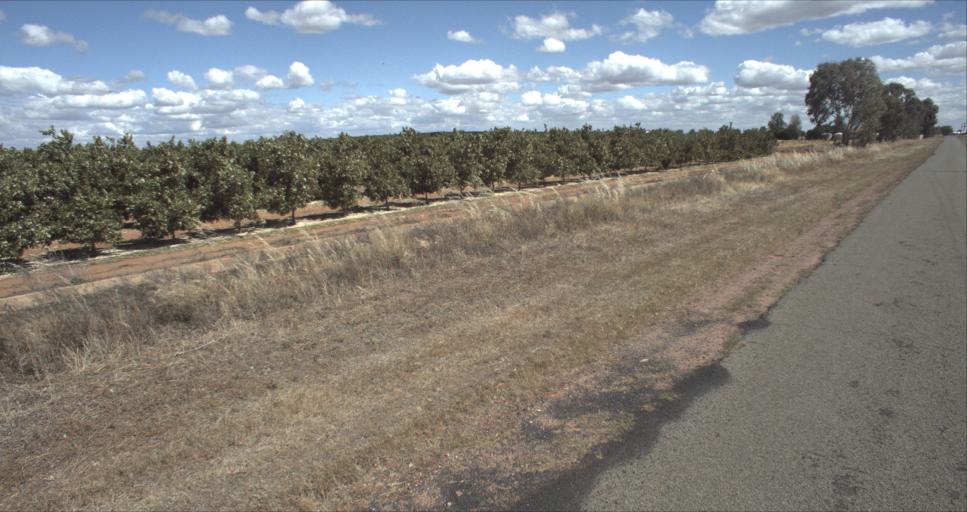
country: AU
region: New South Wales
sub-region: Leeton
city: Leeton
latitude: -34.5146
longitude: 146.2393
